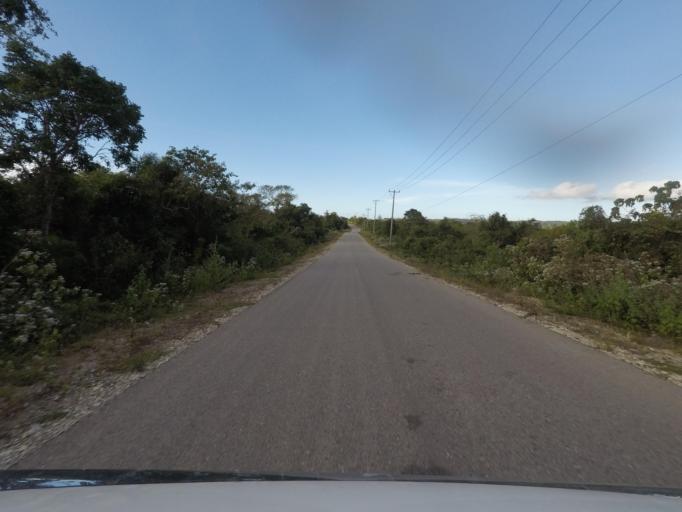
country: TL
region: Lautem
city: Lospalos
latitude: -8.4014
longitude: 127.0035
